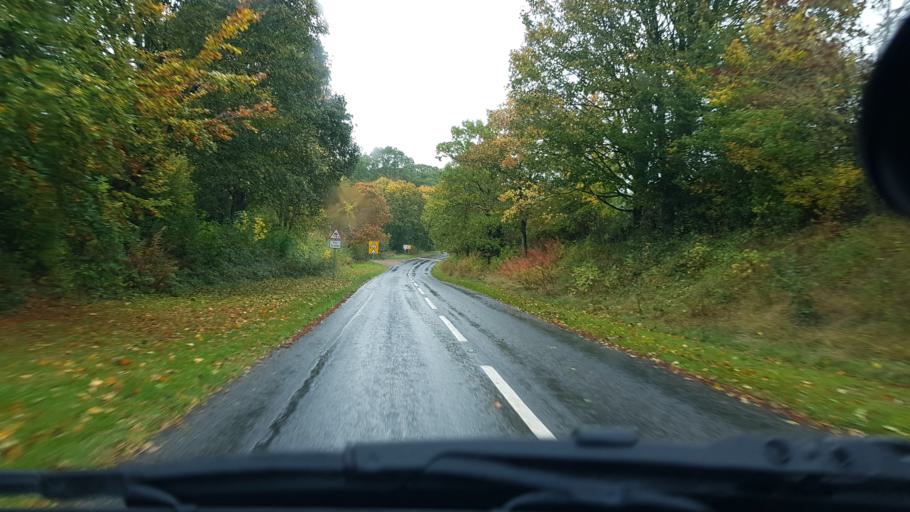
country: GB
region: England
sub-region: Gloucestershire
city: Stow on the Wold
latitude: 51.9375
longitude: -1.7401
